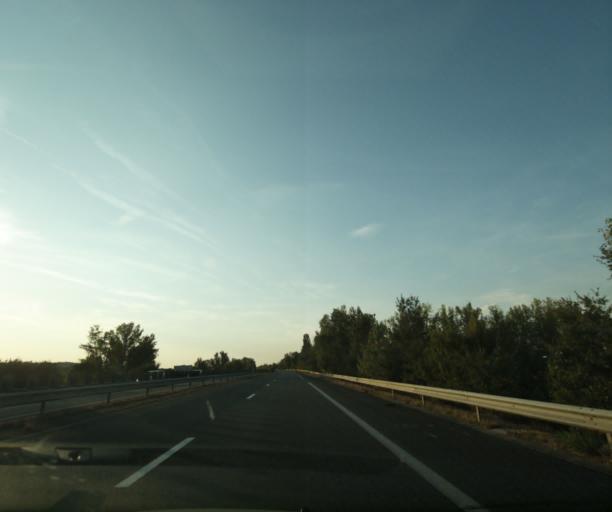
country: FR
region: Aquitaine
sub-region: Departement du Lot-et-Garonne
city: Layrac
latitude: 44.1377
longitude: 0.6714
